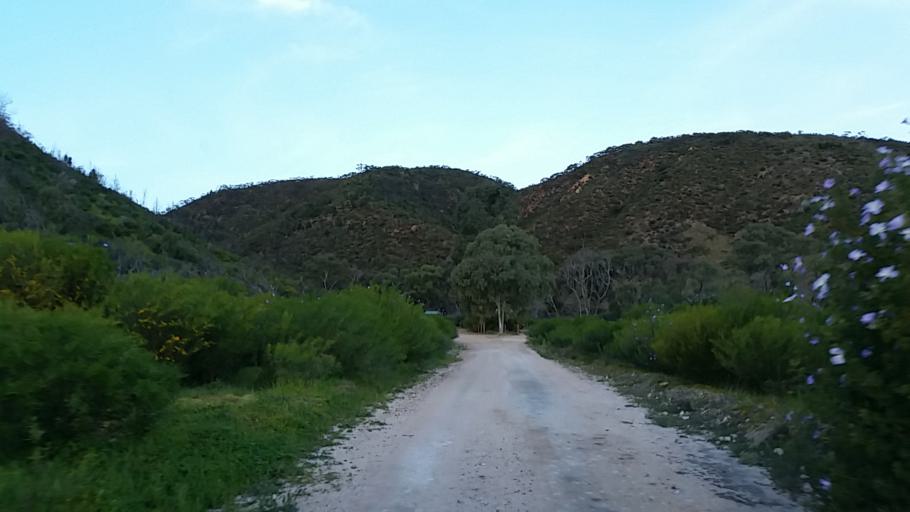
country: AU
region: South Australia
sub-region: Port Pirie City and Dists
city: Port Pirie
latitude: -33.0246
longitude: 138.1019
